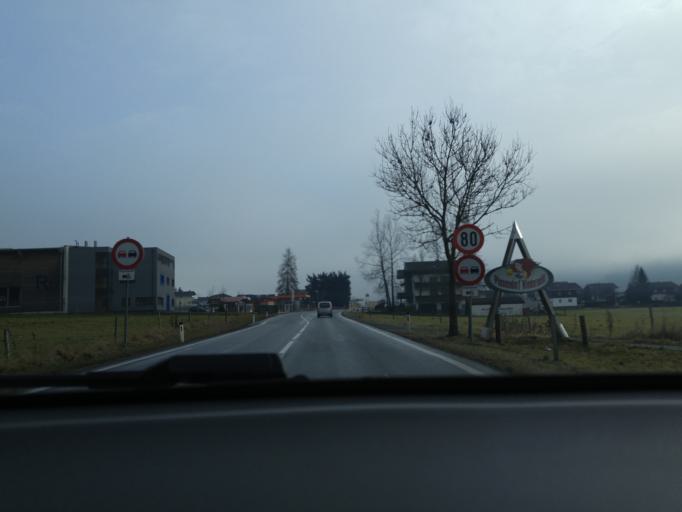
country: AT
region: Salzburg
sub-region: Politischer Bezirk Zell am See
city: Niedernsill
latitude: 47.2848
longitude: 12.6195
